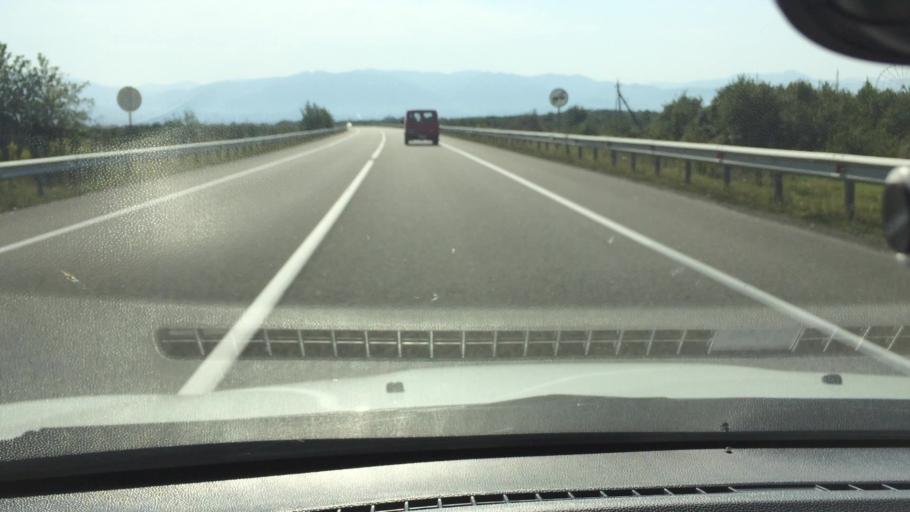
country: GE
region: Guria
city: Urek'i
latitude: 41.9161
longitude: 41.7772
